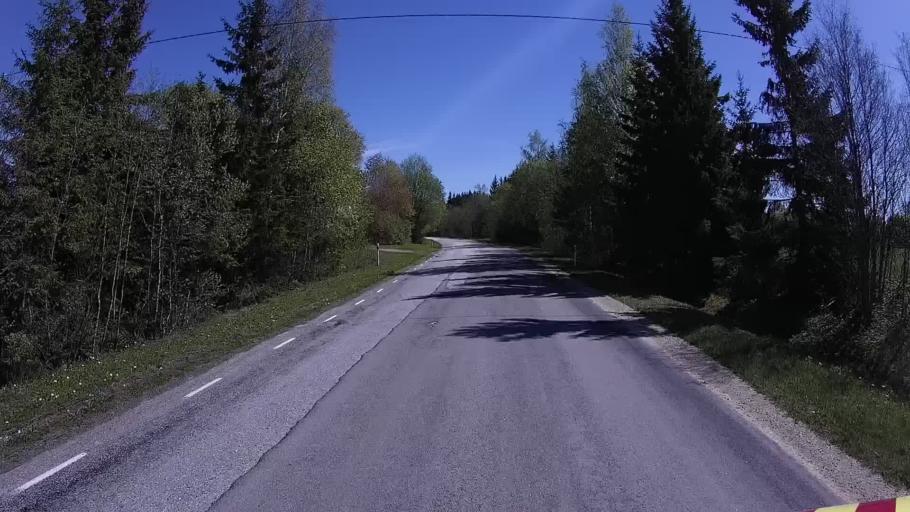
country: EE
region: Raplamaa
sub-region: Kehtna vald
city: Kehtna
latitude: 59.0387
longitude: 25.0408
